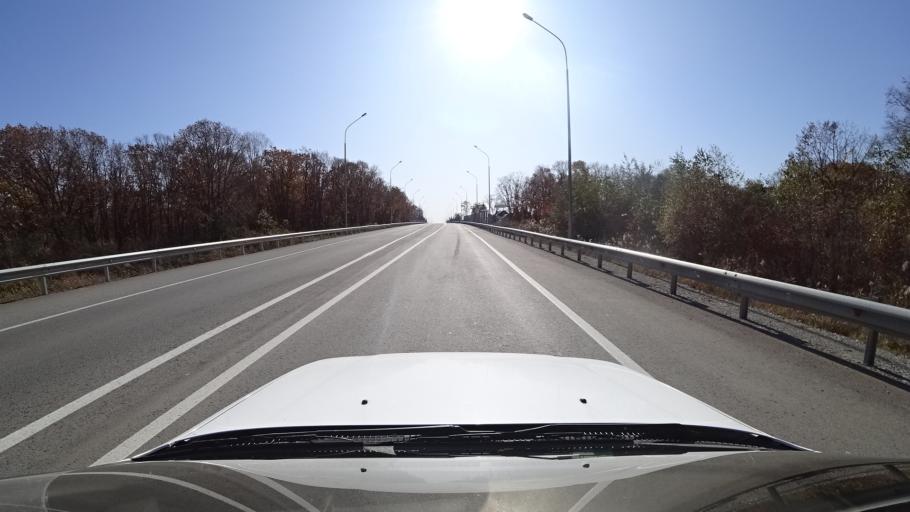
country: RU
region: Primorskiy
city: Dal'nerechensk
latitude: 45.8845
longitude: 133.7302
